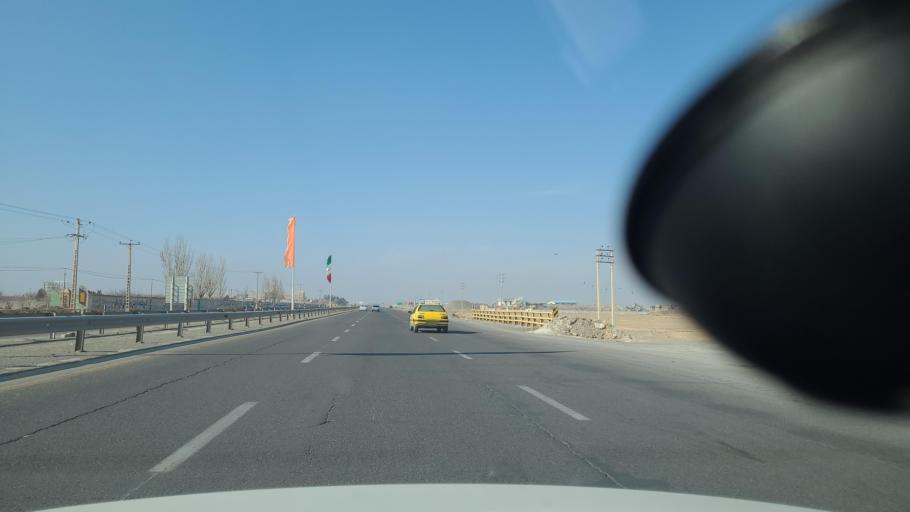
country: IR
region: Razavi Khorasan
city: Fariman
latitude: 35.7096
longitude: 59.8310
